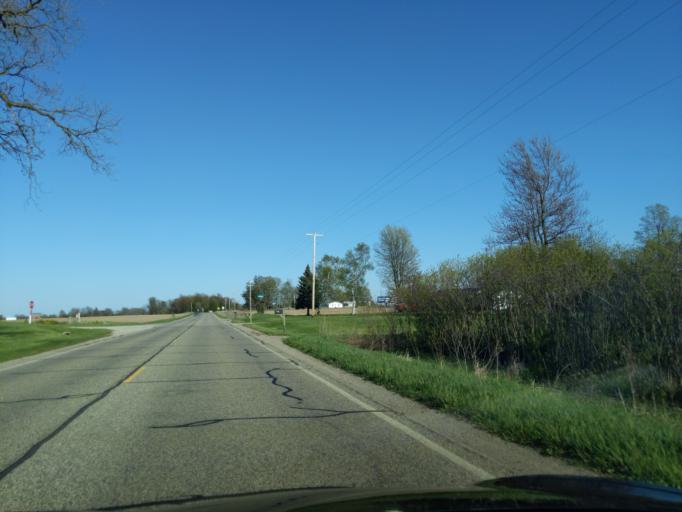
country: US
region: Michigan
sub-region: Ionia County
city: Portland
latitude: 42.8800
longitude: -84.9762
